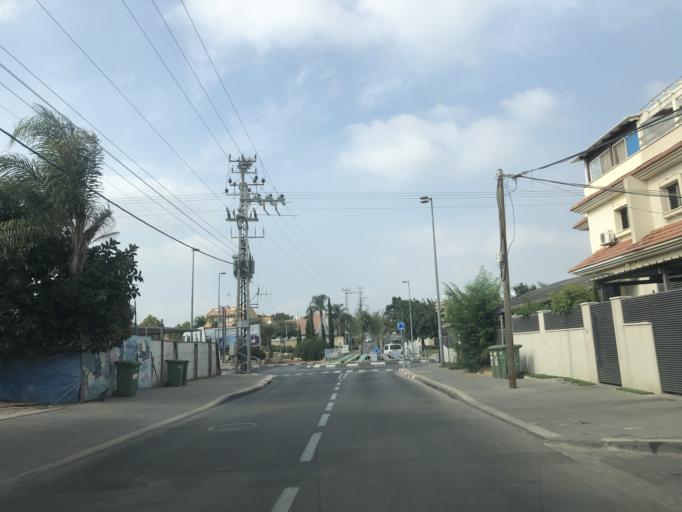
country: IL
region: Central District
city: Rosh Ha'Ayin
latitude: 32.0986
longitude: 34.9496
